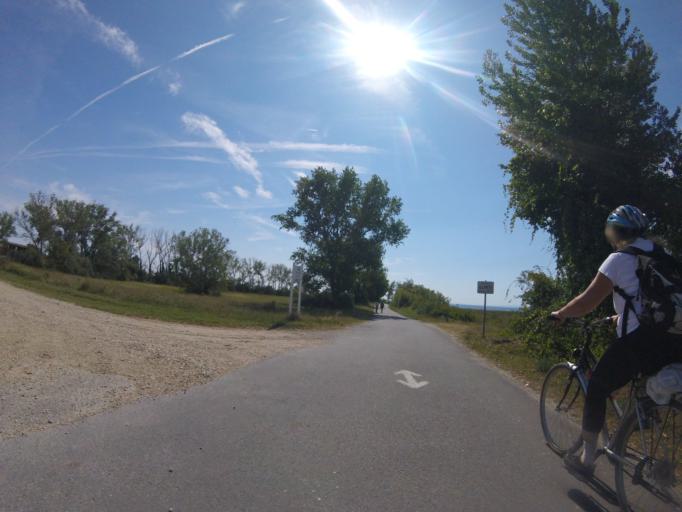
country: AT
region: Burgenland
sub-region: Politischer Bezirk Neusiedl am See
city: Podersdorf am See
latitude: 47.8308
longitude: 16.8044
